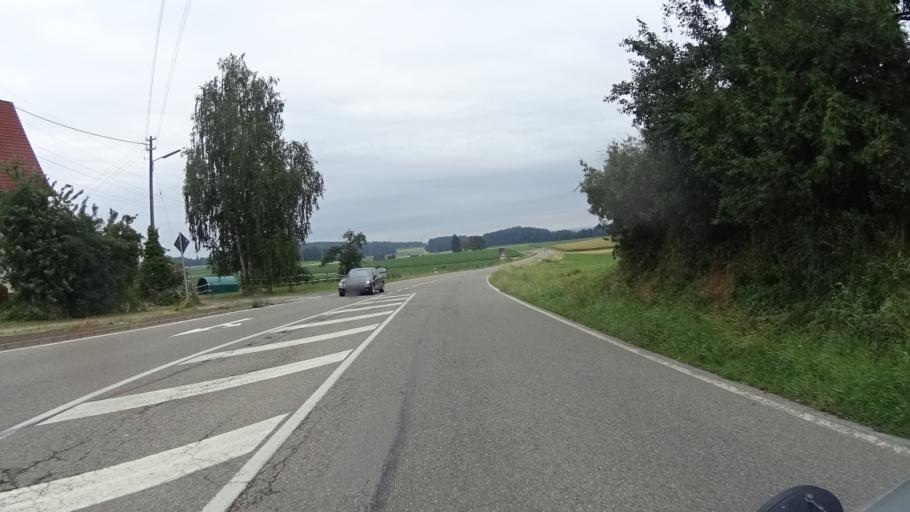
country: DE
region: Bavaria
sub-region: Swabia
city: Kellmunz
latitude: 48.1225
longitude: 10.1325
